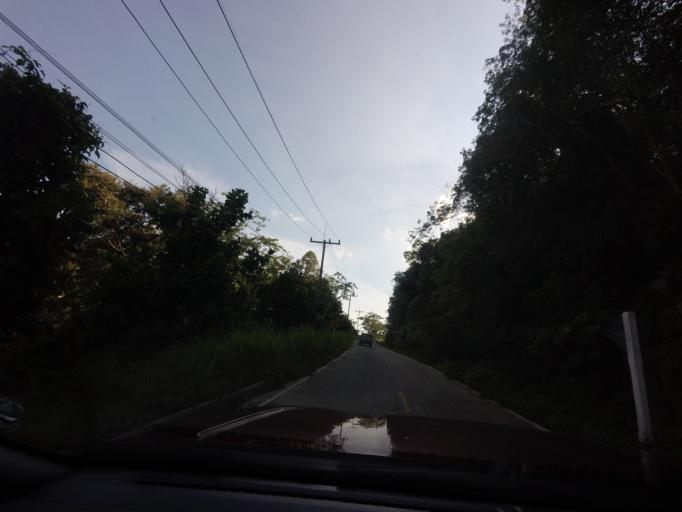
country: TH
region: Yala
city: Than To
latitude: 6.0982
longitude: 101.3119
